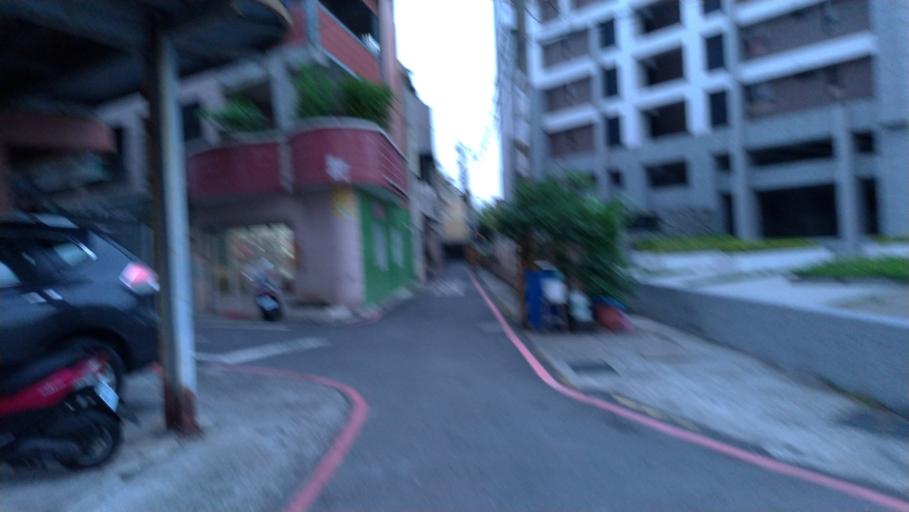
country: TW
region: Taiwan
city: Fengshan
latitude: 22.6536
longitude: 120.3629
